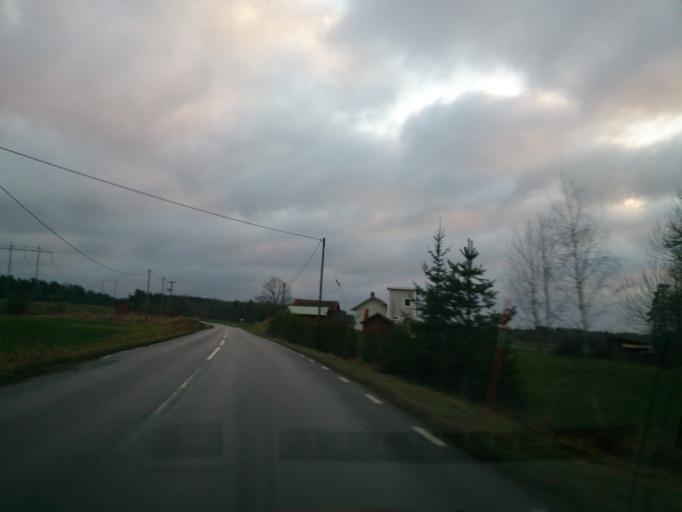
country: SE
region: OEstergoetland
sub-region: Atvidabergs Kommun
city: Atvidaberg
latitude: 58.3687
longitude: 16.0235
